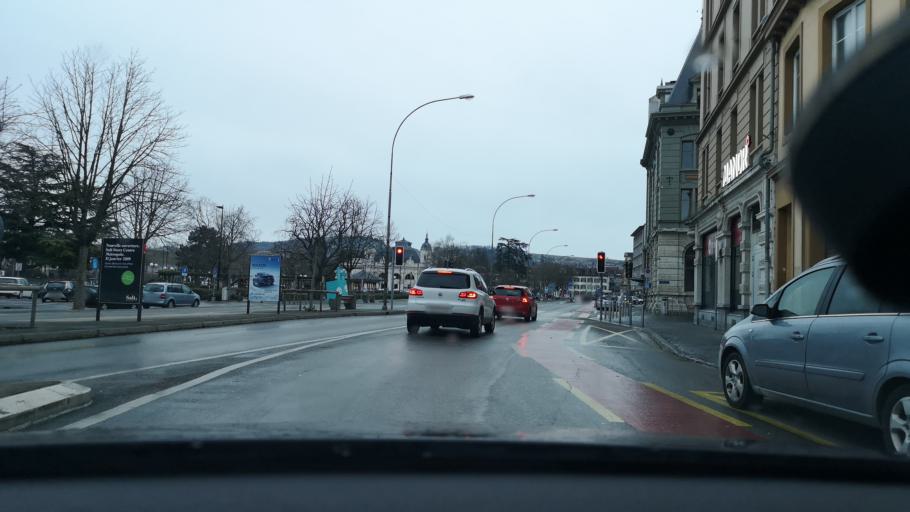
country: CH
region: Vaud
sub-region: Jura-Nord vaudois District
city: Yverdon-les-Bains
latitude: 46.7806
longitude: 6.6388
